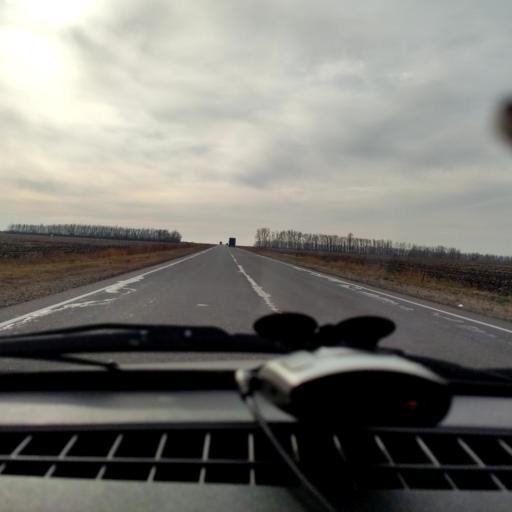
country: RU
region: Voronezj
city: Strelitsa
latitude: 51.4854
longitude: 38.9626
